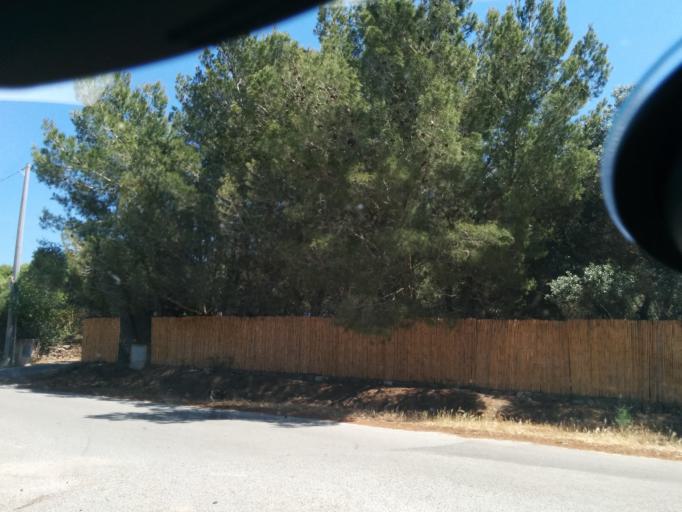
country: IT
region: Sardinia
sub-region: Provincia di Carbonia-Iglesias
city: Calasetta
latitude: 39.0772
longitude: 8.3636
